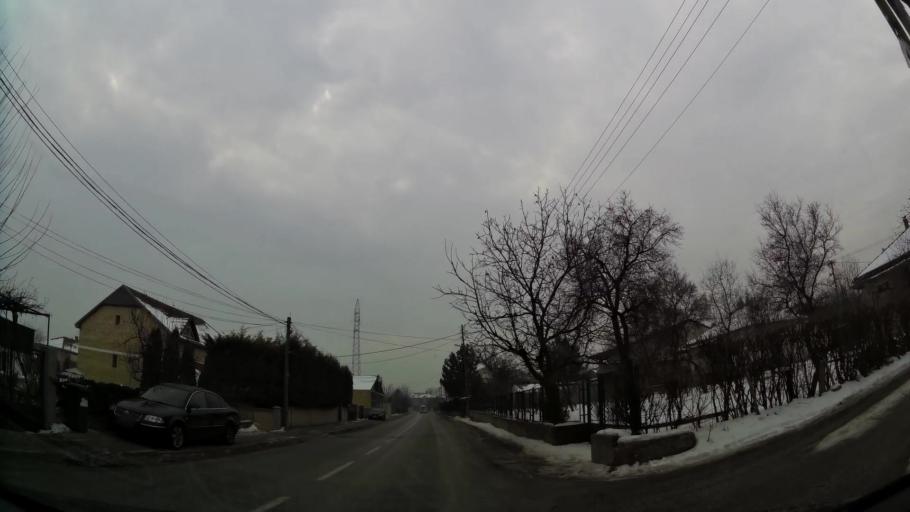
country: MK
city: Kondovo
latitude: 42.0416
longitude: 21.3473
